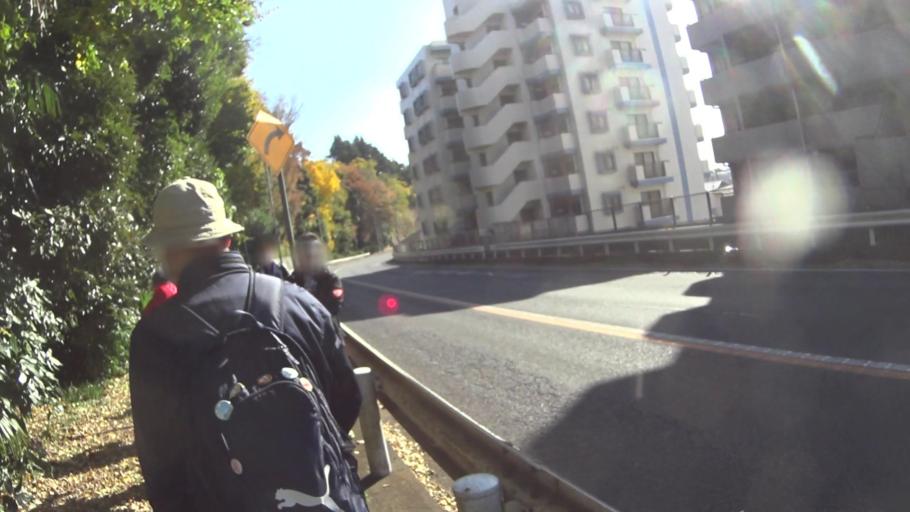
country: JP
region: Ibaraki
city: Mito-shi
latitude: 36.3713
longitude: 140.4829
